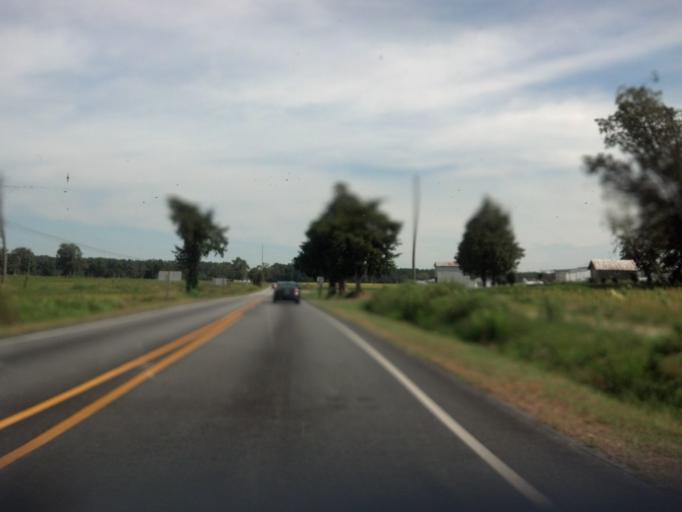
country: US
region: North Carolina
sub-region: Greene County
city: Maury
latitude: 35.4826
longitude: -77.6373
